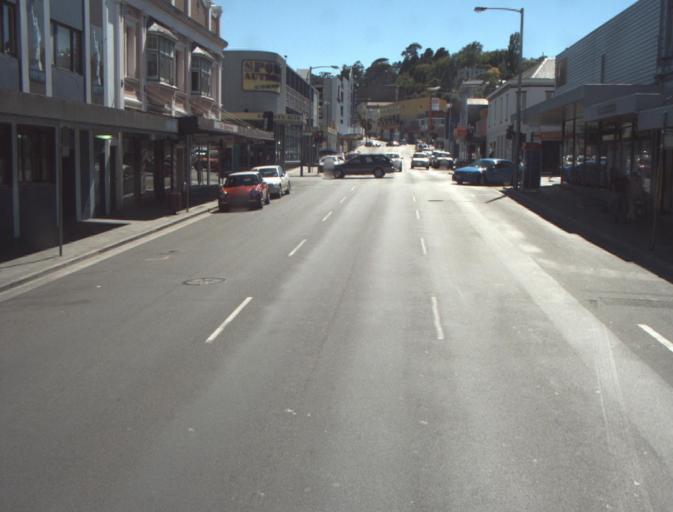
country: AU
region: Tasmania
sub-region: Launceston
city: Launceston
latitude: -41.4389
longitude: 147.1392
